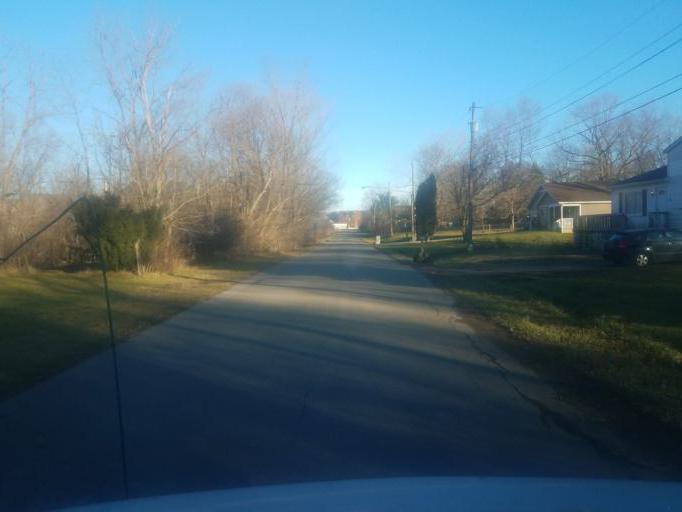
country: US
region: Ohio
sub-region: Richland County
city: Mansfield
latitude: 40.7894
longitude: -82.5318
